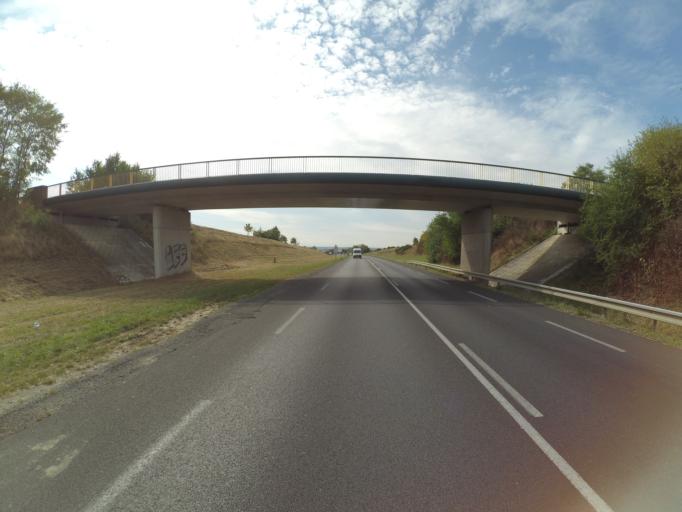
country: FR
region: Pays de la Loire
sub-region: Departement de Maine-et-Loire
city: Distre
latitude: 47.2454
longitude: -0.1073
